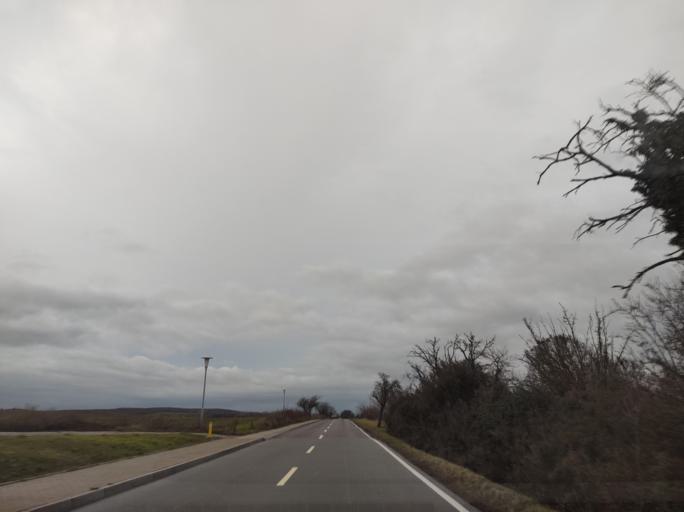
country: DE
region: Saxony-Anhalt
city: Roblingen am See
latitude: 51.4481
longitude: 11.6774
